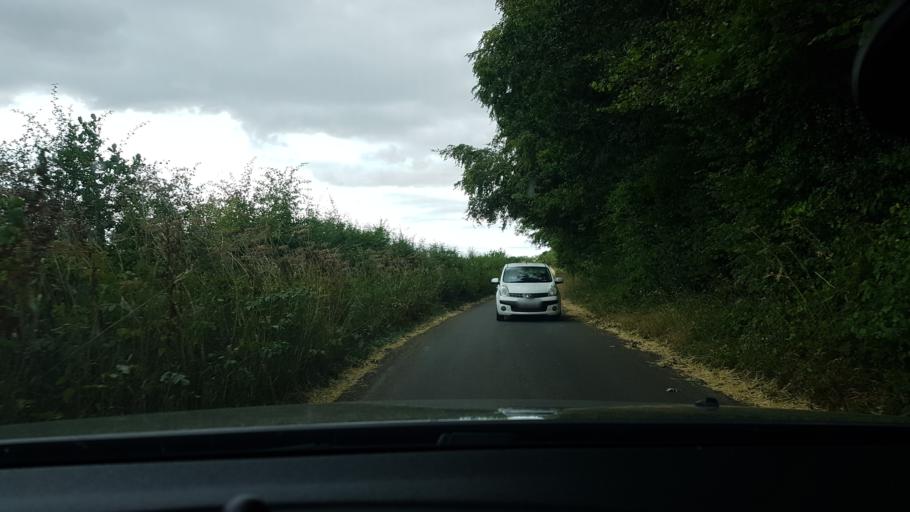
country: GB
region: England
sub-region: West Berkshire
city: Lambourn
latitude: 51.4718
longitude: -1.5091
